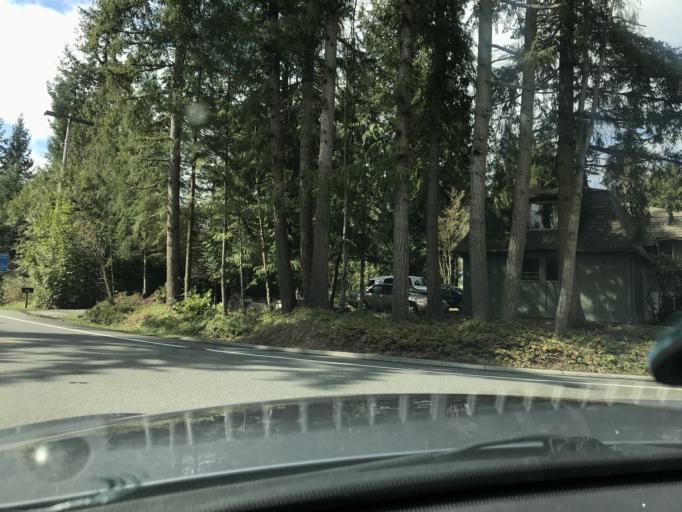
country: US
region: Washington
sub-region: King County
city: City of Sammamish
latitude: 47.5811
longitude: -122.0516
